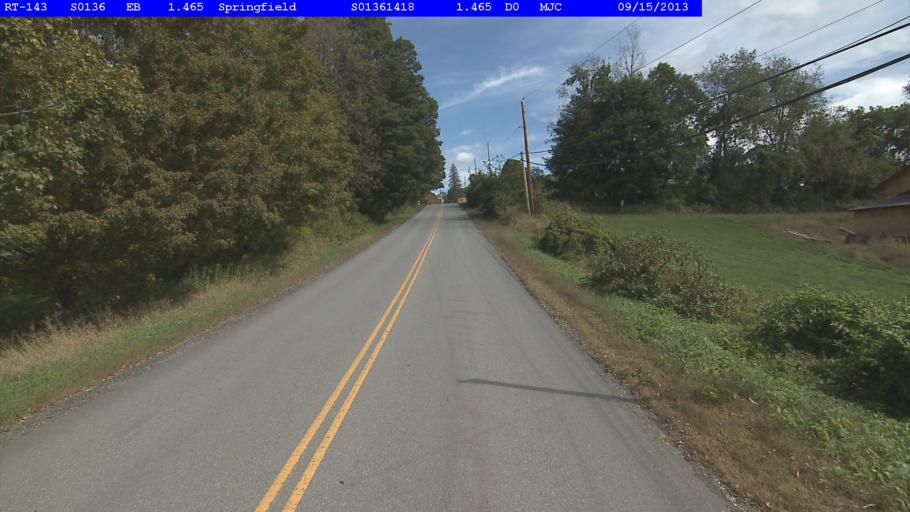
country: US
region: Vermont
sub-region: Windsor County
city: Springfield
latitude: 43.2919
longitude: -72.4587
